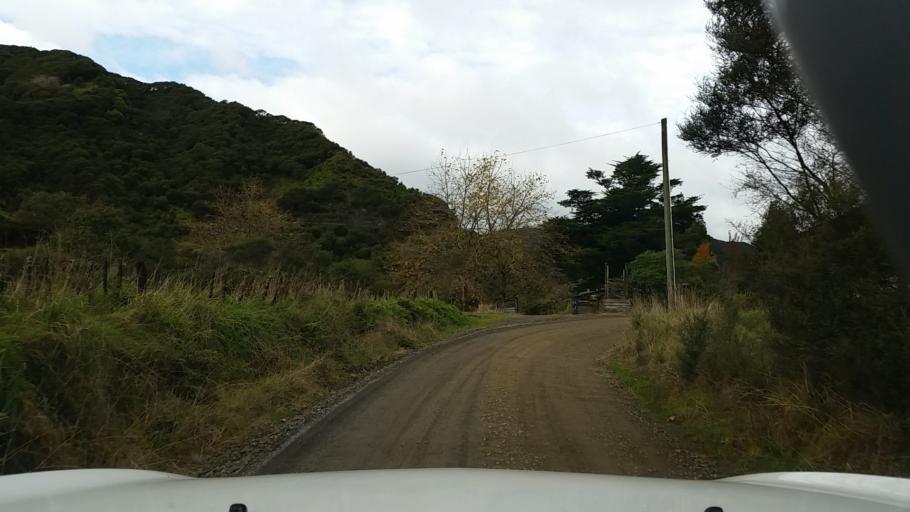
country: NZ
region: Taranaki
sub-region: New Plymouth District
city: Waitara
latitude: -38.8913
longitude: 174.7354
